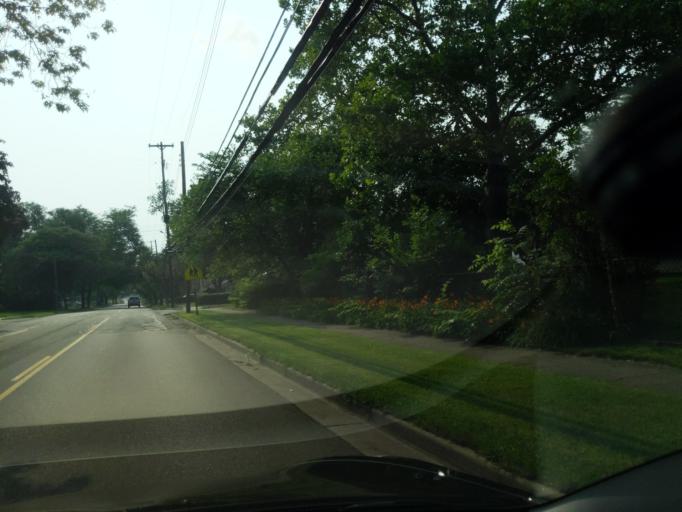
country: US
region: Michigan
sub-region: Jackson County
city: Jackson
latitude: 42.2401
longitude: -84.4252
